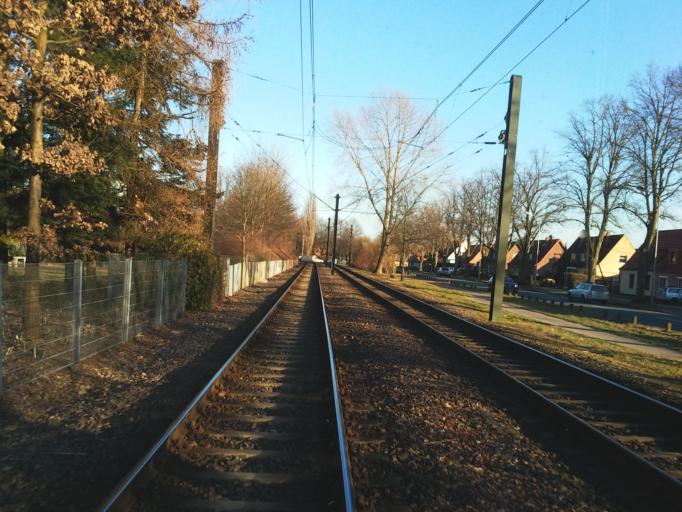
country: DE
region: Mecklenburg-Vorpommern
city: Dierkow-Neu
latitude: 54.1027
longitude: 12.1634
